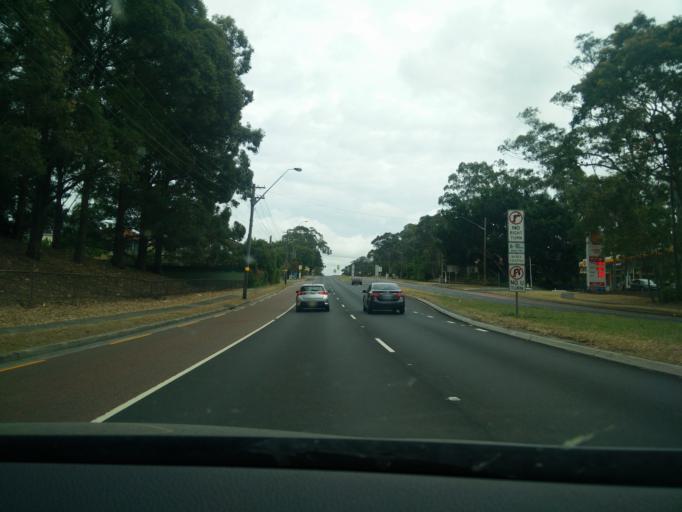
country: AU
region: New South Wales
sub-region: Ryde
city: Marsfield
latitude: -33.7759
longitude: 151.1055
